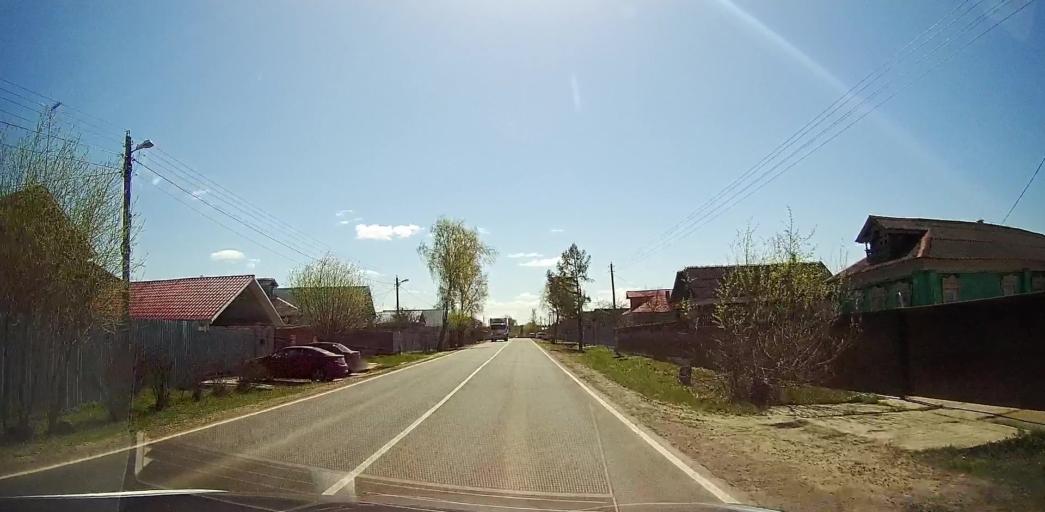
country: RU
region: Moskovskaya
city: Beloozerskiy
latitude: 55.5122
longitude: 38.4319
